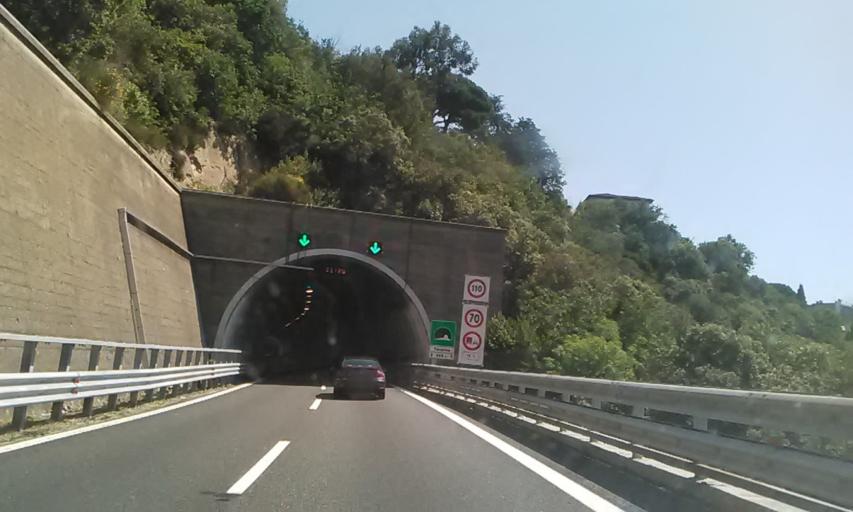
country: IT
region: Liguria
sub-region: Provincia di Savona
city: Savona
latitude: 44.3241
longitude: 8.4906
